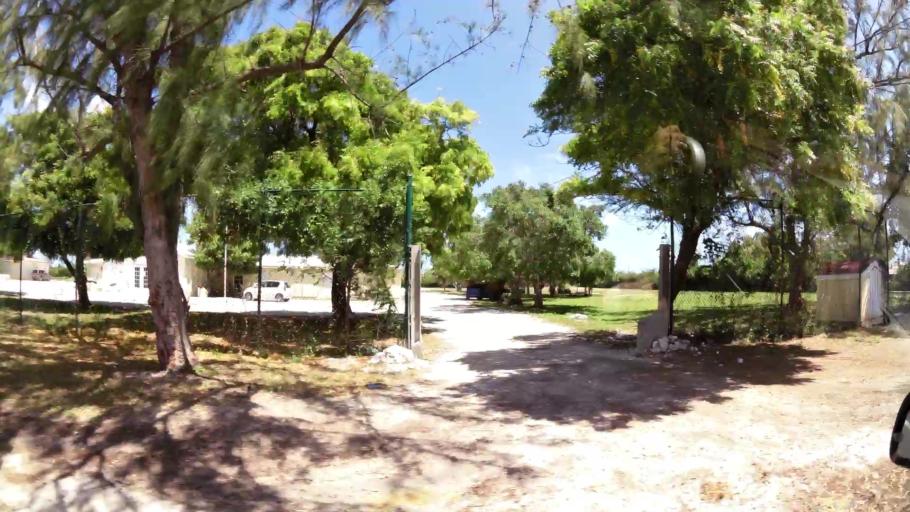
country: TC
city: Cockburn Town
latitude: 21.4520
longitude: -71.1439
